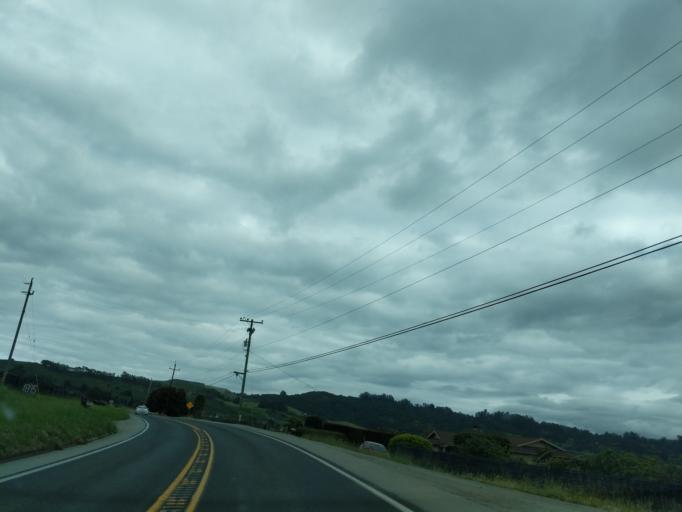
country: US
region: California
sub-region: San Benito County
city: Aromas
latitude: 36.9059
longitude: -121.6492
